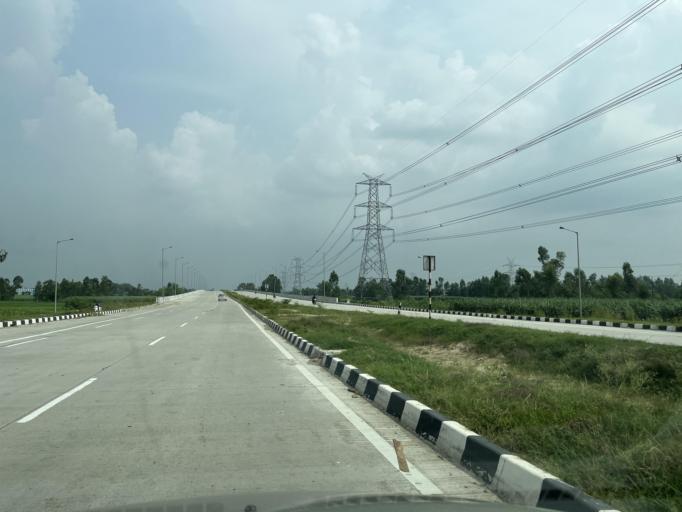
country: IN
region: Uttarakhand
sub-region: Udham Singh Nagar
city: Jaspur
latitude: 29.2974
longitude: 78.8379
